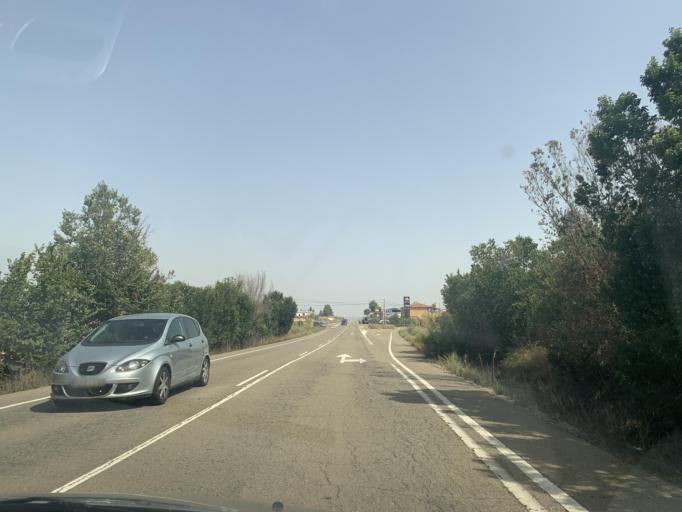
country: ES
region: Aragon
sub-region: Provincia de Zaragoza
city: Belchite
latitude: 41.3076
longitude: -0.7429
